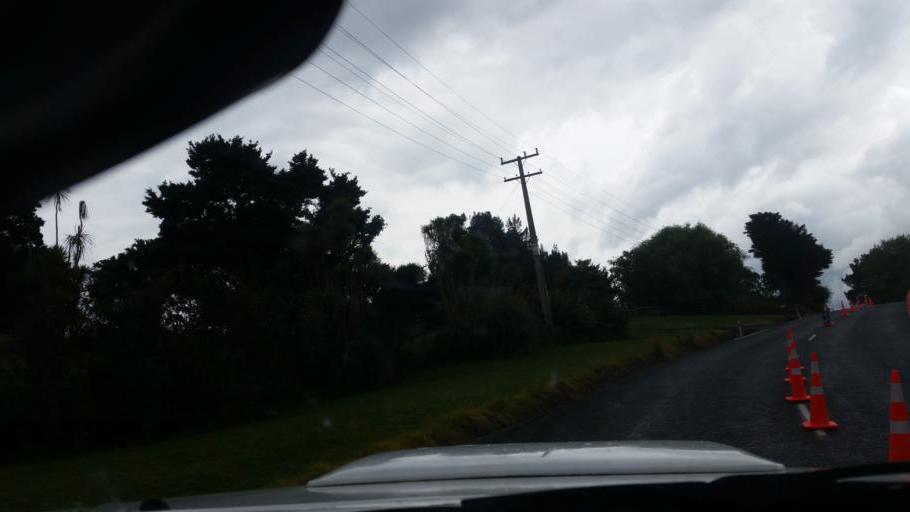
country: NZ
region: Auckland
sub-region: Auckland
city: Wellsford
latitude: -36.1489
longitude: 174.2206
